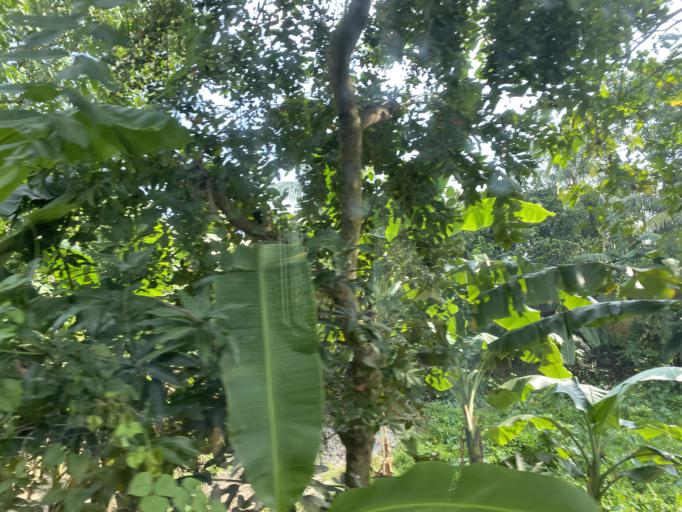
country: BD
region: Dhaka
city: Bhairab Bazar
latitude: 23.9654
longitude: 91.1168
